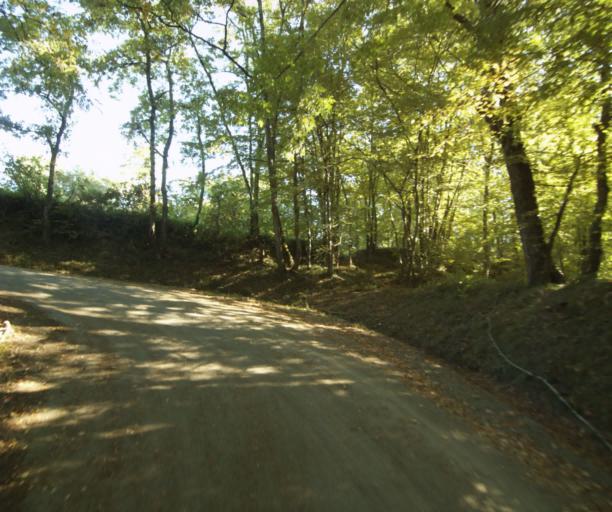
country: FR
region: Midi-Pyrenees
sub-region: Departement du Gers
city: Gondrin
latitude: 43.8141
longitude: 0.2242
